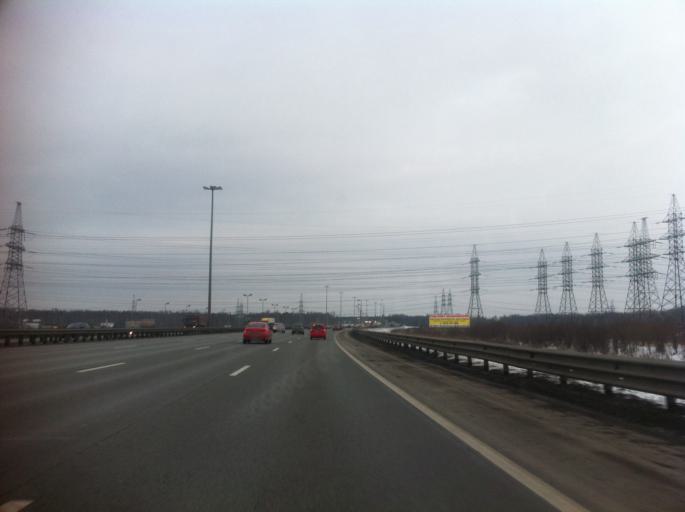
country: RU
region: Leningrad
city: Rybatskoye
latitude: 59.9034
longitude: 30.5265
